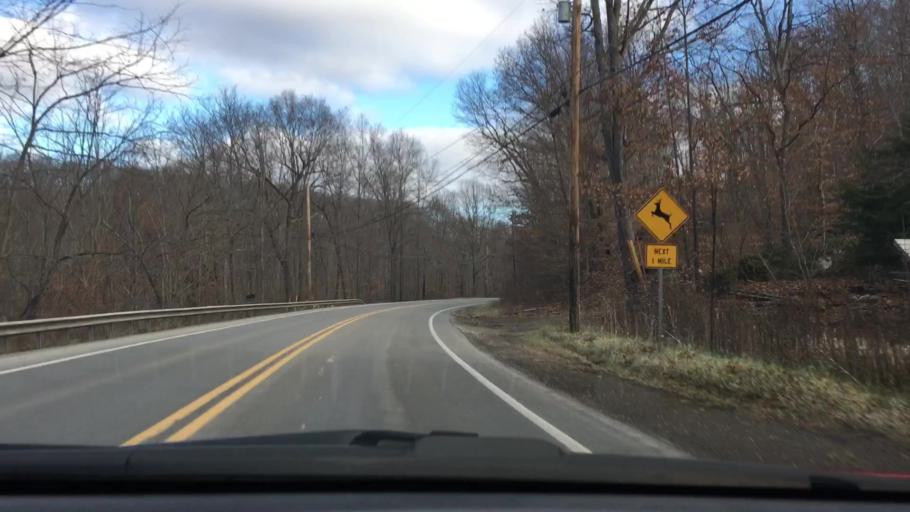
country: US
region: Pennsylvania
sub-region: Westmoreland County
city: Avonmore
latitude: 40.6253
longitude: -79.4289
